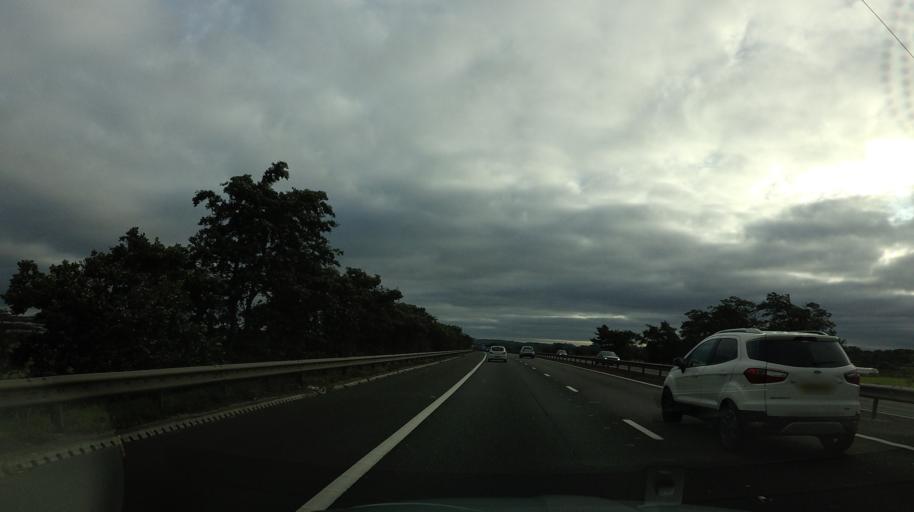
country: GB
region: Scotland
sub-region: West Lothian
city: Broxburn
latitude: 55.9215
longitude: -3.4705
